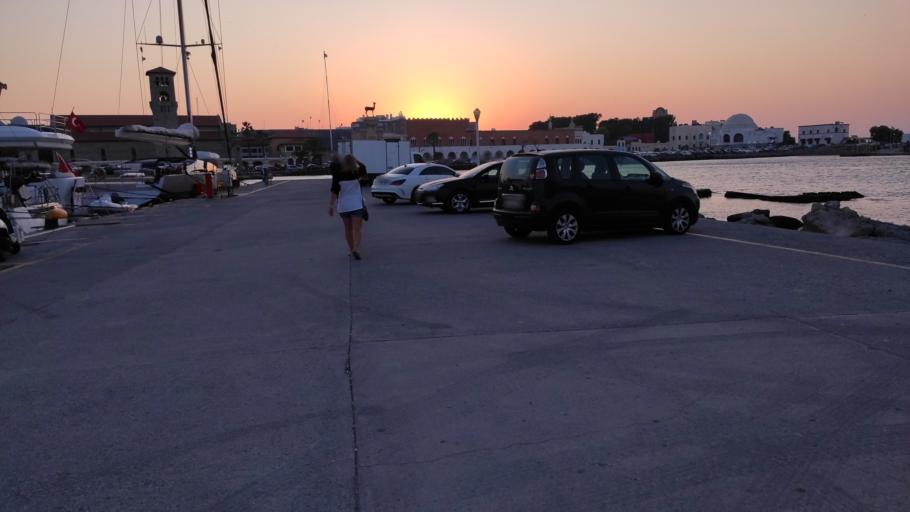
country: GR
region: South Aegean
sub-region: Nomos Dodekanisou
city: Rodos
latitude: 36.4510
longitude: 28.2274
